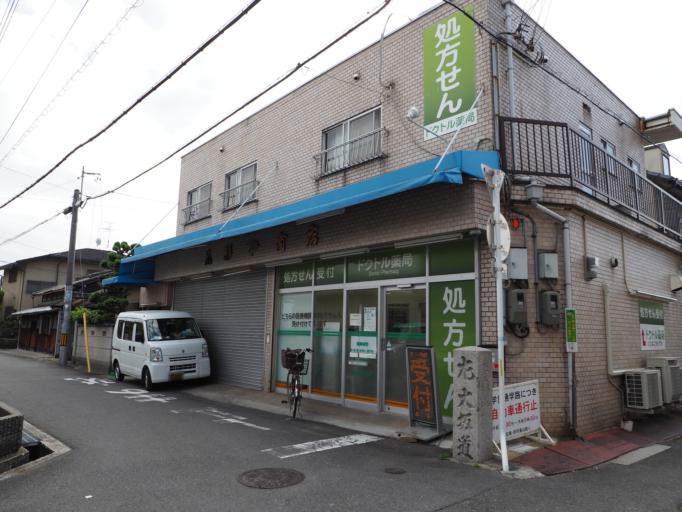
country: JP
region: Osaka
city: Daitocho
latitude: 34.6740
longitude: 135.6271
